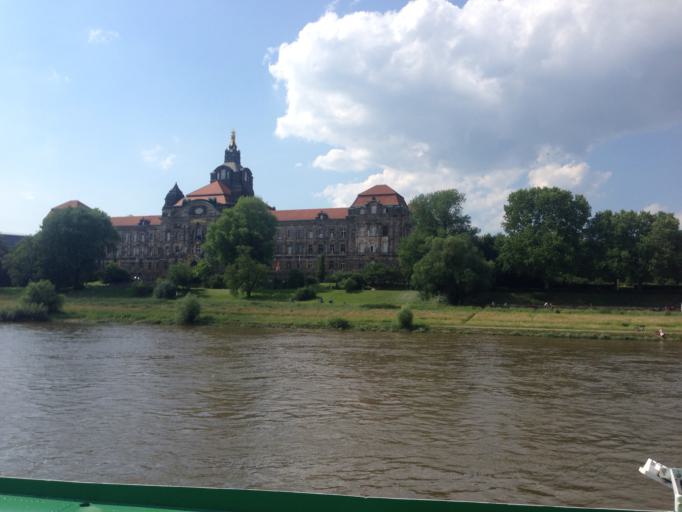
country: DE
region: Saxony
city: Dresden
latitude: 51.0557
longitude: 13.7513
